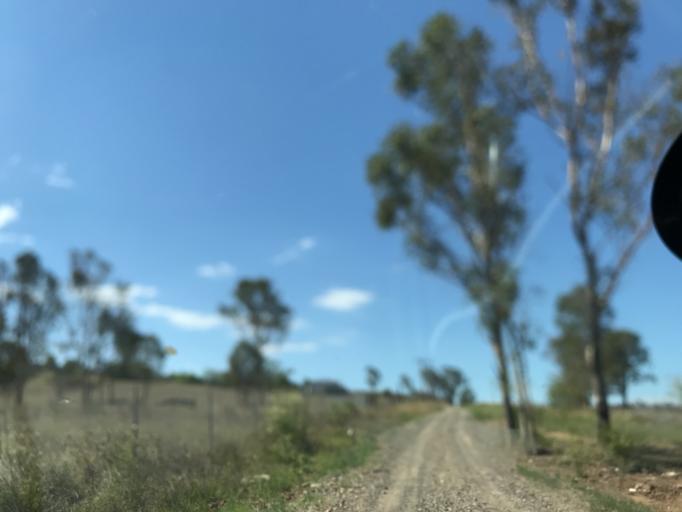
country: AU
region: New South Wales
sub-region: Penrith Municipality
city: Kingswood Park
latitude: -33.7964
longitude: 150.7368
